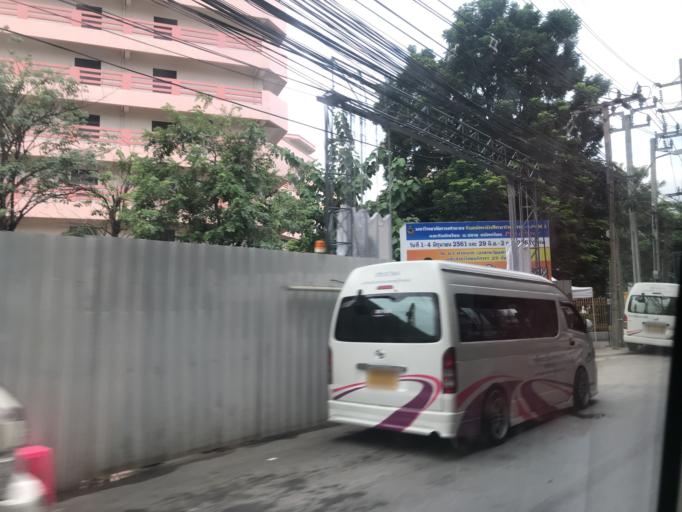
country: TH
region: Bangkok
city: Wang Thonglang
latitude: 13.7586
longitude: 100.6169
